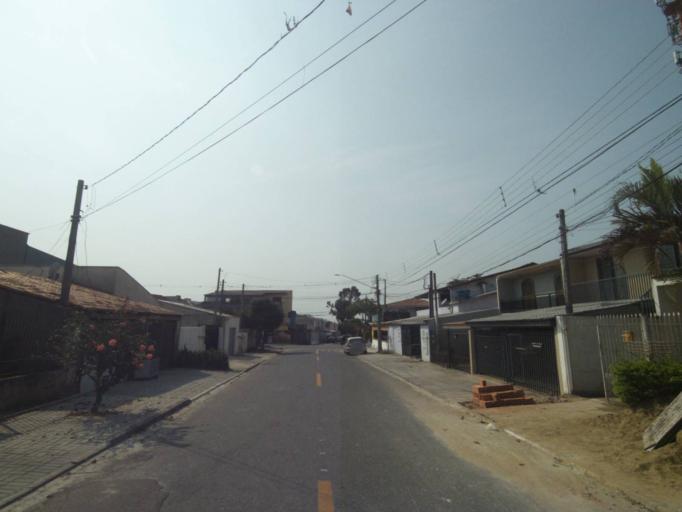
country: BR
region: Parana
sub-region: Sao Jose Dos Pinhais
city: Sao Jose dos Pinhais
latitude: -25.4872
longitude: -49.2045
